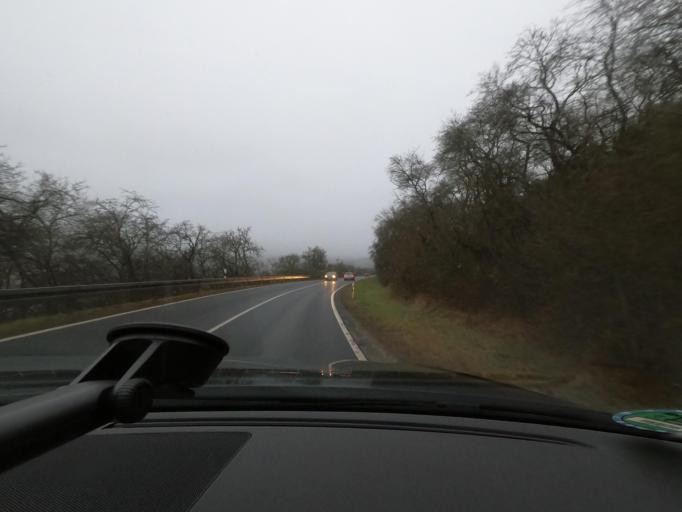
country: DE
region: Thuringia
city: Behringen
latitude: 50.7755
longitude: 11.0012
